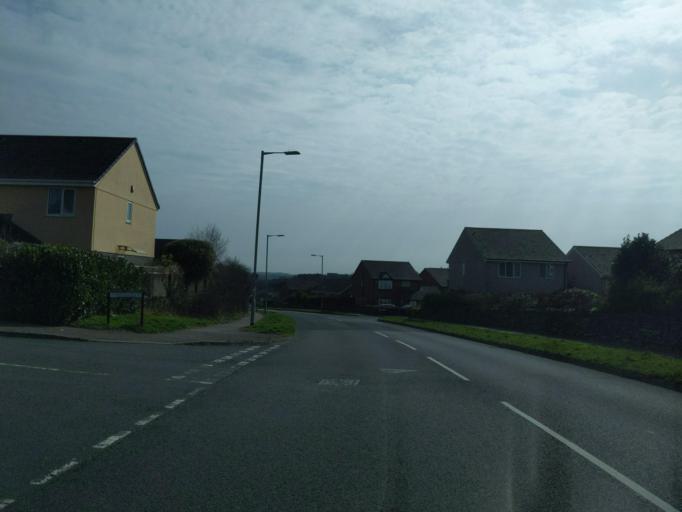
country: GB
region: England
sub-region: Cornwall
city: Saltash
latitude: 50.4124
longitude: -4.2424
